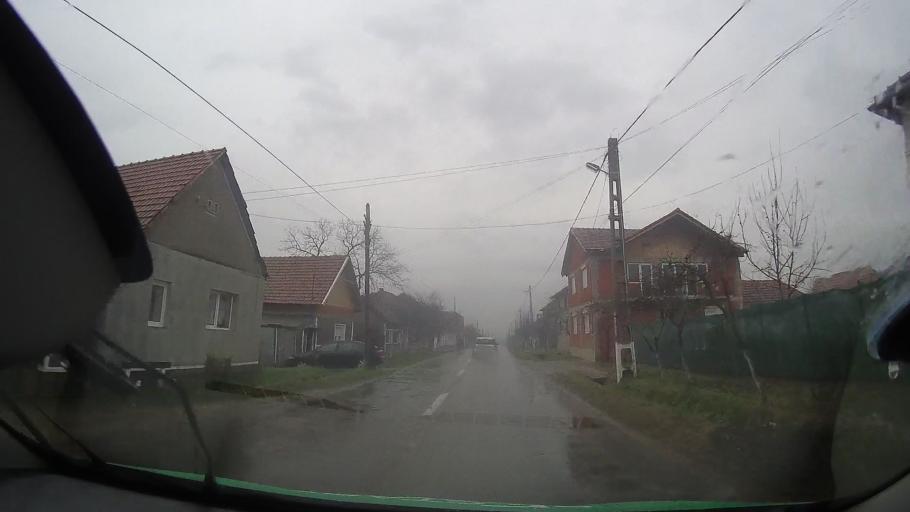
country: RO
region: Bihor
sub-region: Comuna Holod
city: Vintere
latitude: 46.7645
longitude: 22.1511
